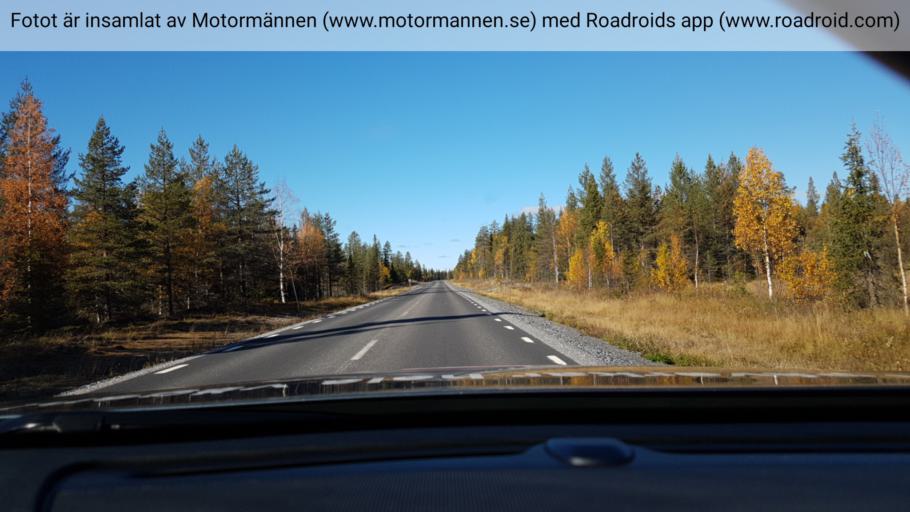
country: SE
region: Norrbotten
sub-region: Gallivare Kommun
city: Gaellivare
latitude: 66.8656
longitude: 20.9861
